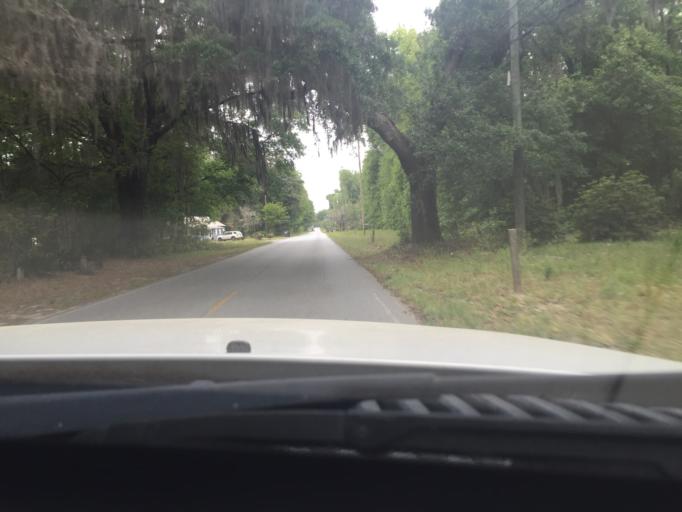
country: US
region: Georgia
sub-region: Chatham County
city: Georgetown
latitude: 31.9705
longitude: -81.2444
